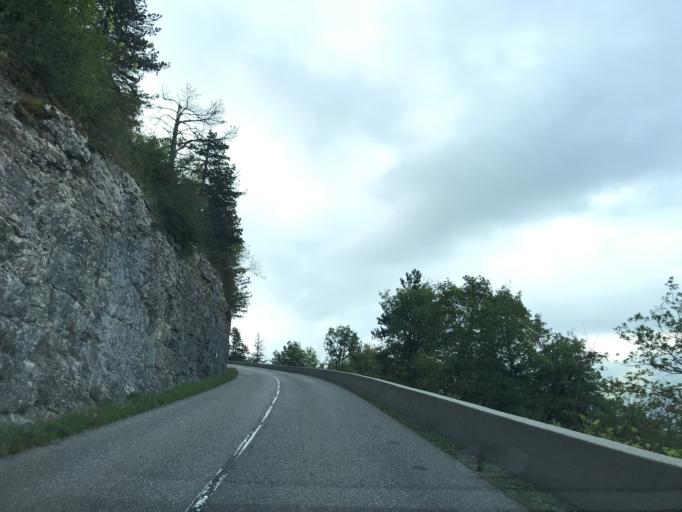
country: FR
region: Rhone-Alpes
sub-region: Departement de la Haute-Savoie
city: Talloires
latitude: 45.8444
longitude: 6.2211
